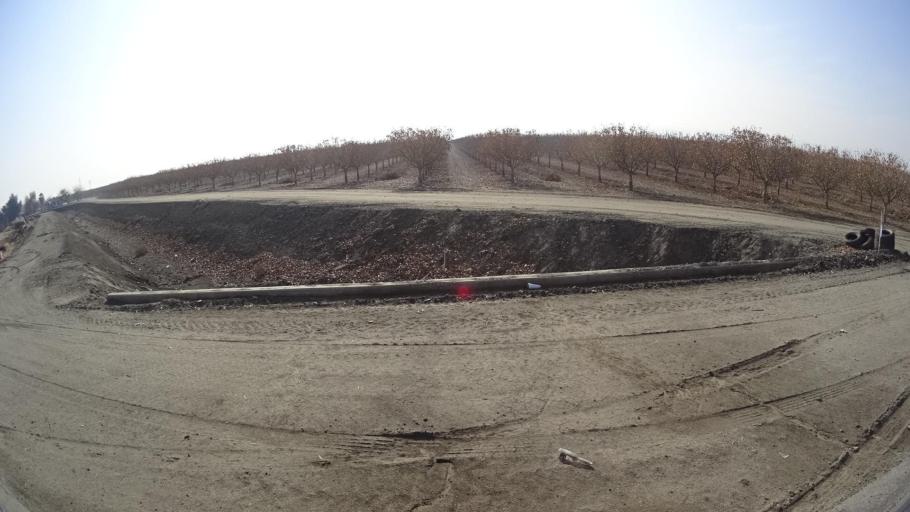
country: US
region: California
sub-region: Kern County
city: Buttonwillow
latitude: 35.3546
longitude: -119.4235
